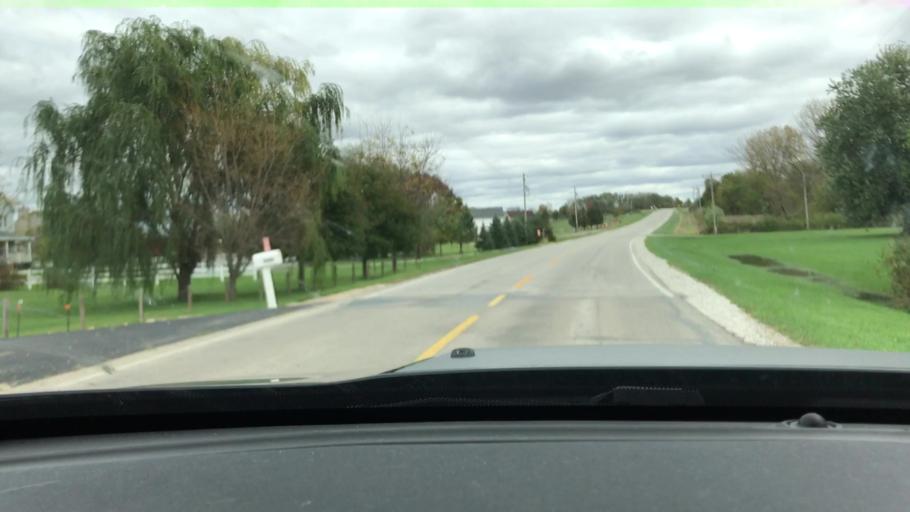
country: US
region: Illinois
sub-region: LaSalle County
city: Sheridan
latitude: 41.5299
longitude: -88.6740
